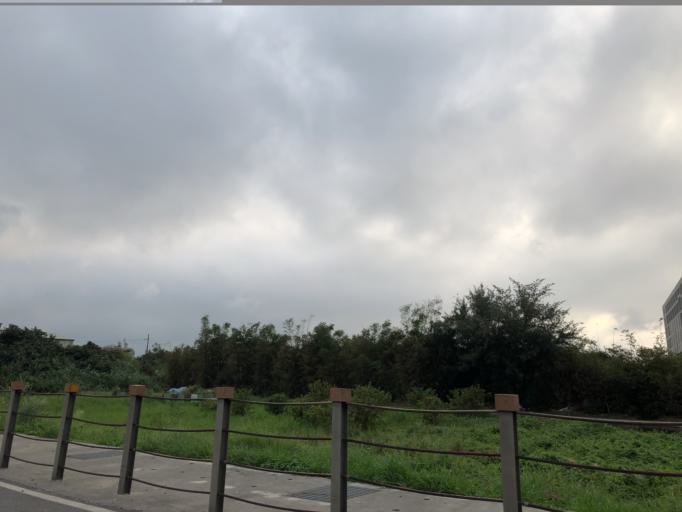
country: TW
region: Taiwan
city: Taoyuan City
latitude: 25.1033
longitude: 121.2477
